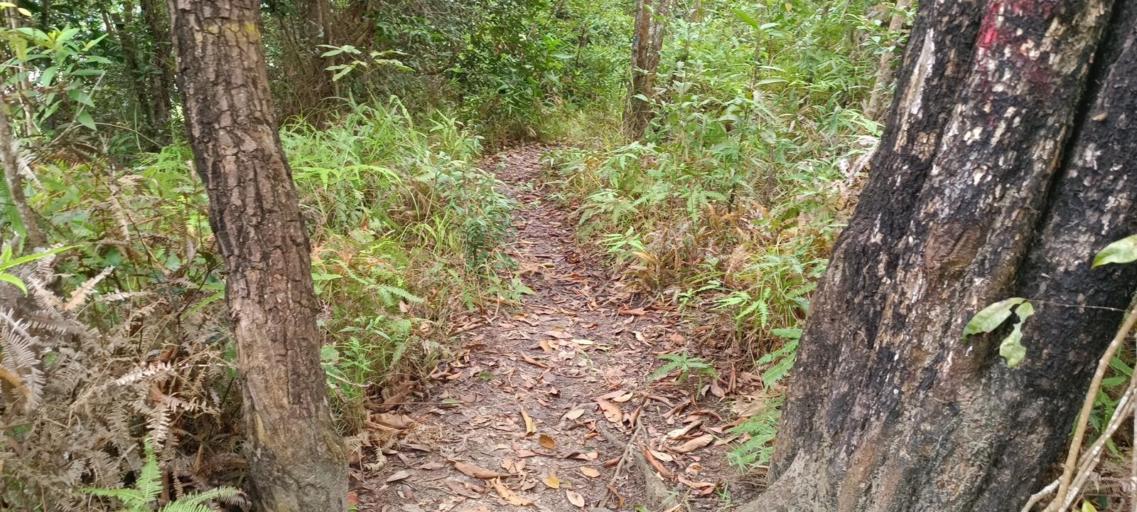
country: MY
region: Penang
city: George Town
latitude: 5.3863
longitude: 100.2884
